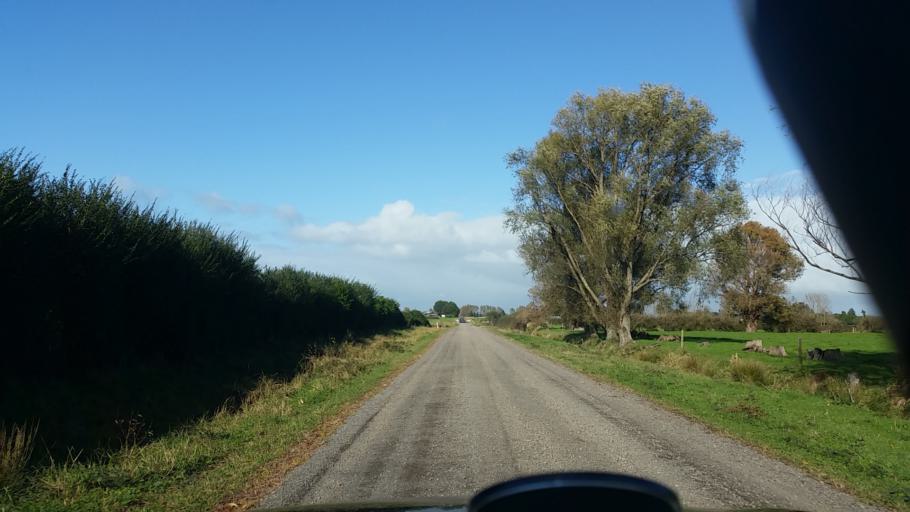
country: NZ
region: Bay of Plenty
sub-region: Western Bay of Plenty District
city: Katikati
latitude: -37.5899
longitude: 175.7132
